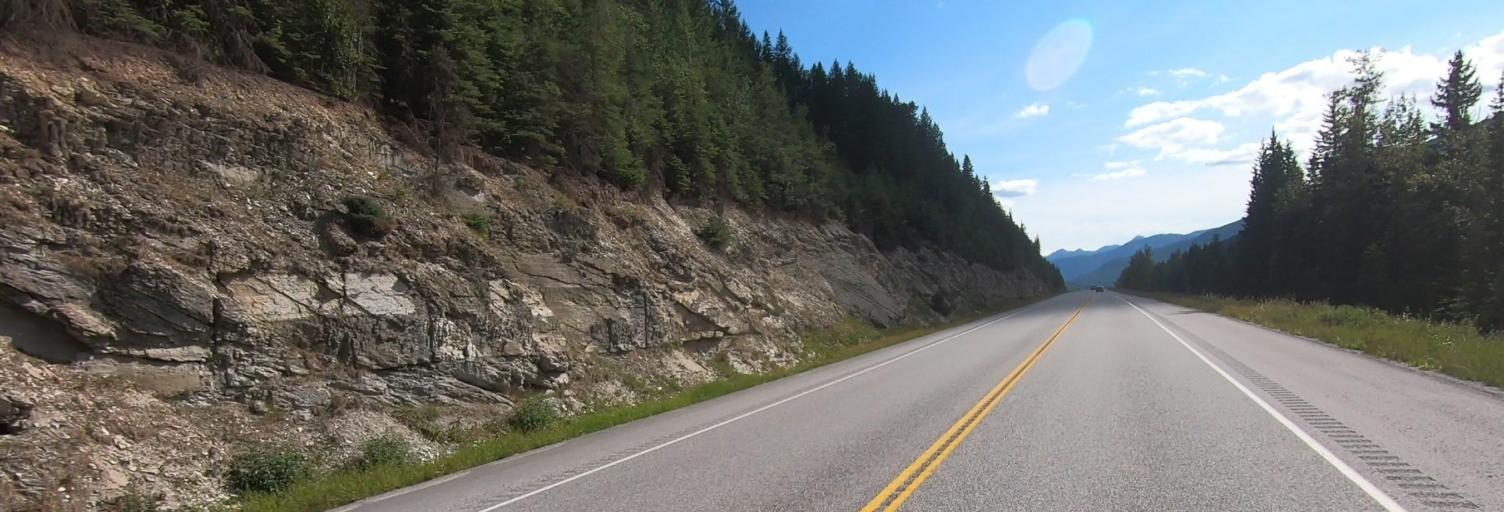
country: CA
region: Alberta
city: Lake Louise
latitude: 51.3207
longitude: -116.5756
